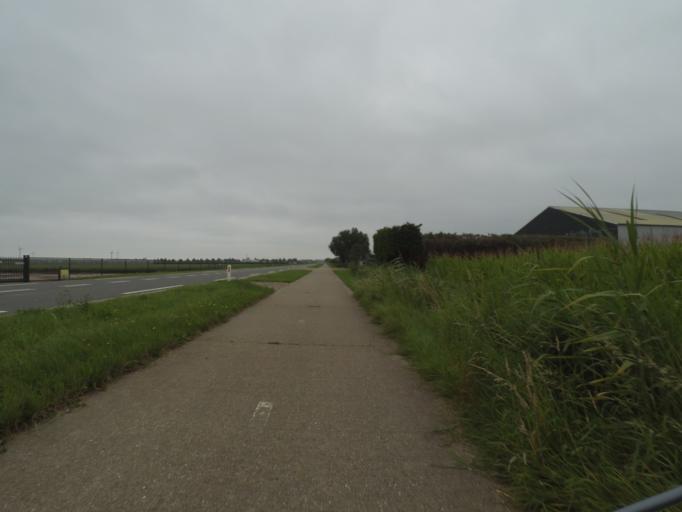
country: NL
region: Flevoland
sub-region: Gemeente Zeewolde
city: Zeewolde
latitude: 52.3686
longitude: 5.4633
